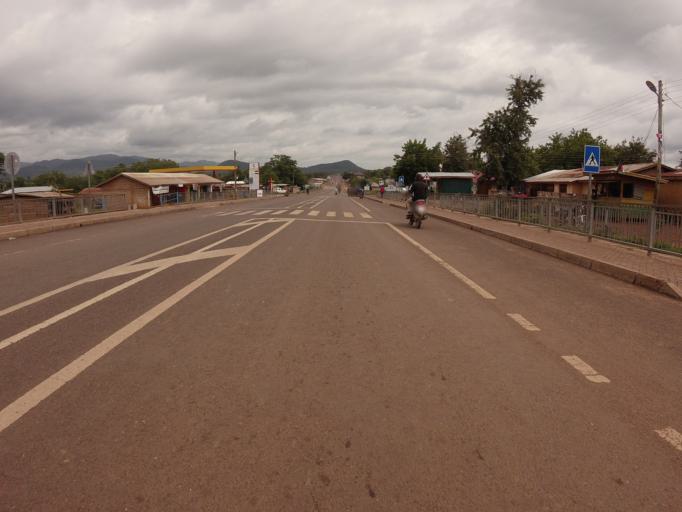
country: TG
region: Centrale
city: Sotouboua
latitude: 8.2576
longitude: 0.5223
